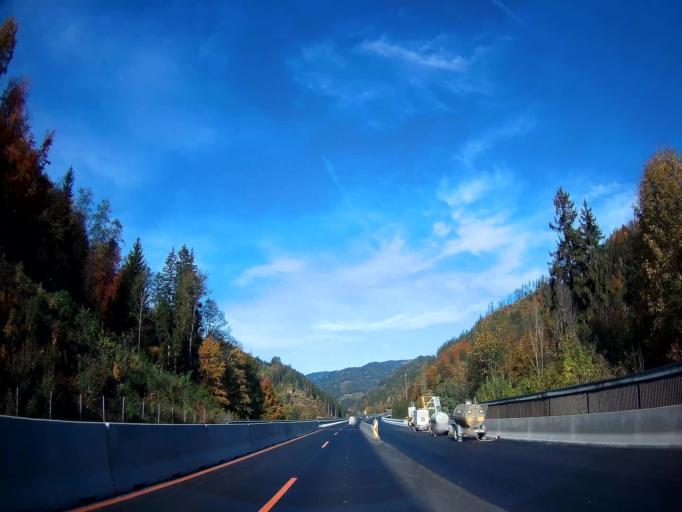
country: AT
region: Styria
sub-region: Politischer Bezirk Graz-Umgebung
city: Ubelbach
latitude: 47.2292
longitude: 15.2183
